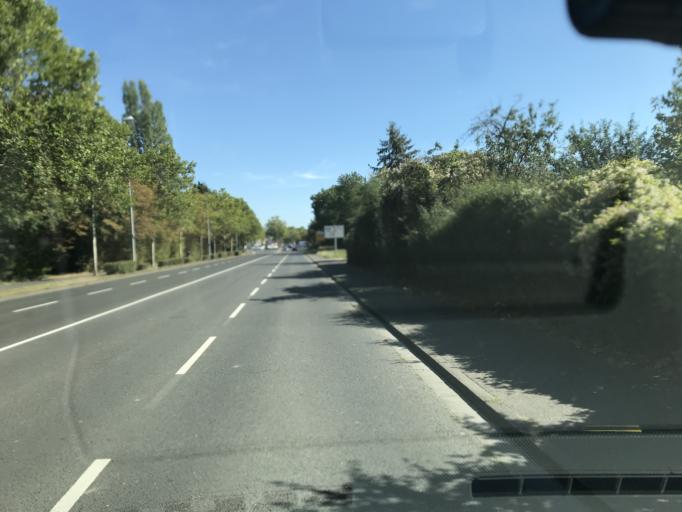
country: DE
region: Rheinland-Pfalz
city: Mainz
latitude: 50.0207
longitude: 8.2852
